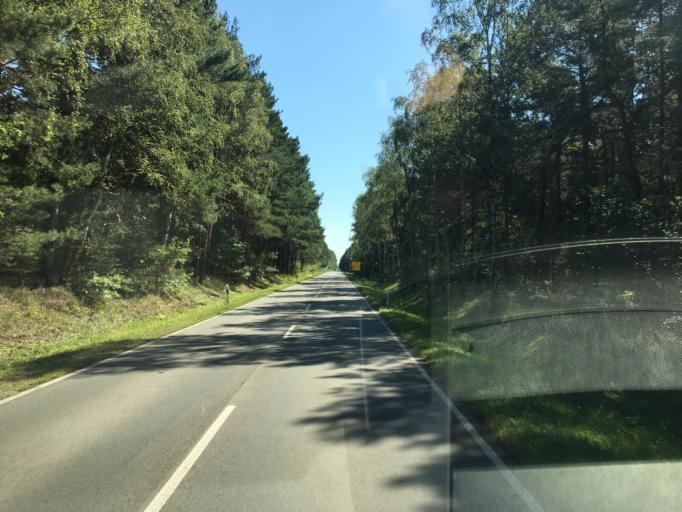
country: DE
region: Brandenburg
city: Welzow
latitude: 51.5389
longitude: 14.1876
